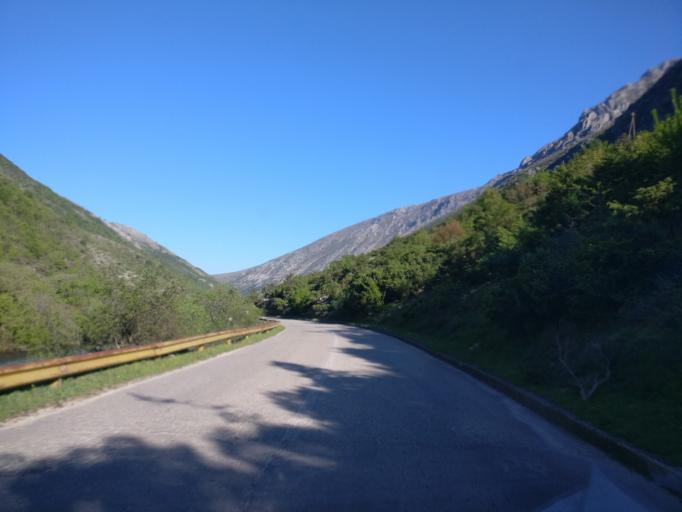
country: BA
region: Federation of Bosnia and Herzegovina
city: Stolac
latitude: 43.0807
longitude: 18.0126
